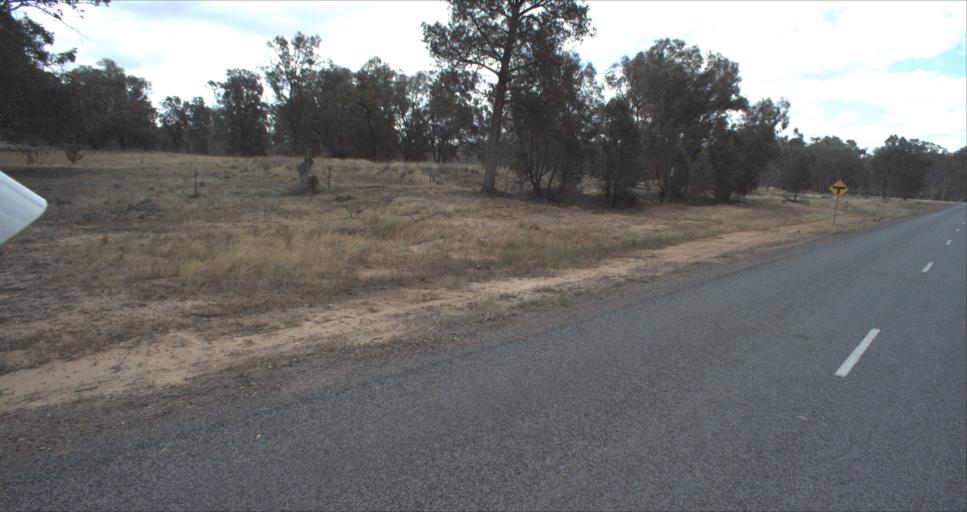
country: AU
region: New South Wales
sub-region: Leeton
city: Leeton
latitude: -34.6453
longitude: 146.3523
